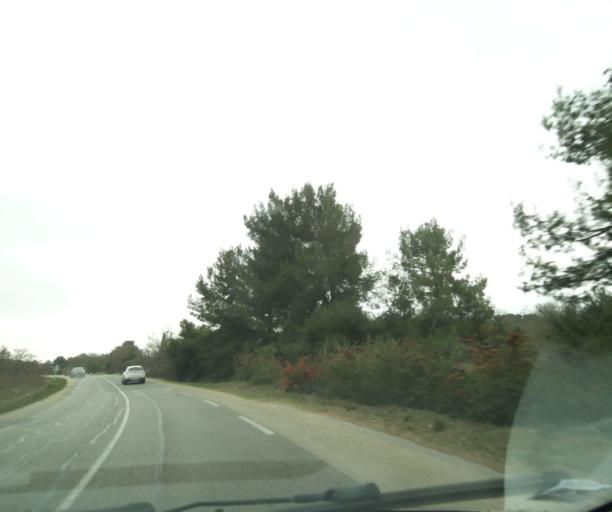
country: FR
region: Provence-Alpes-Cote d'Azur
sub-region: Departement des Bouches-du-Rhone
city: Peyrolles-en-Provence
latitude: 43.6439
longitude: 5.6062
